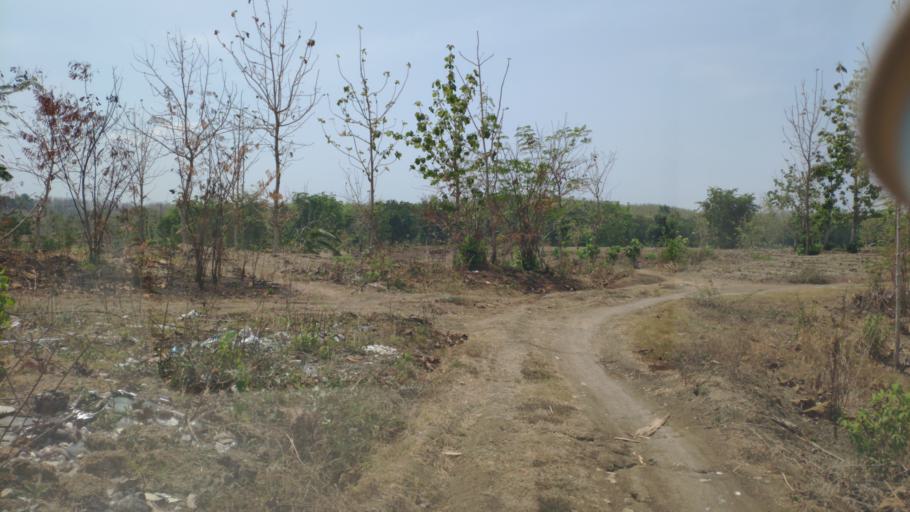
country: ID
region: Central Java
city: Watulumbung
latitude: -7.0216
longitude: 111.5055
